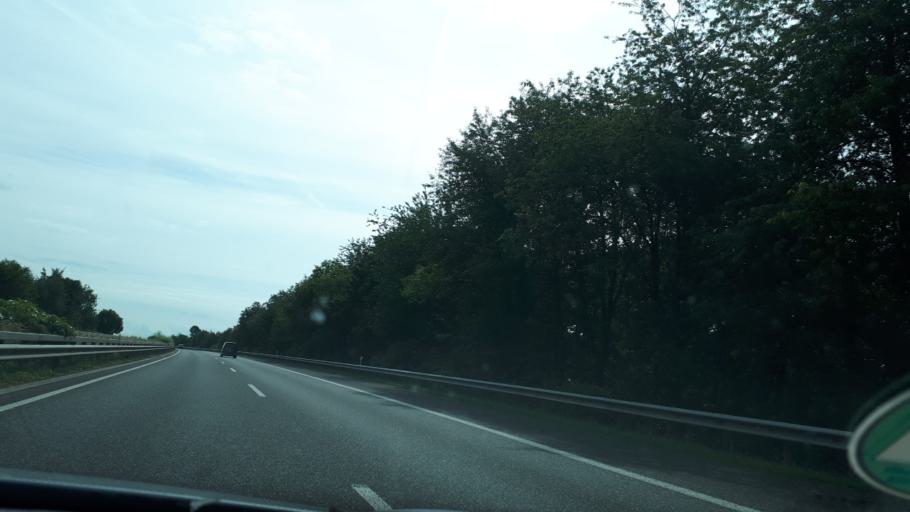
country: DE
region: Rheinland-Pfalz
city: Eulgem
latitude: 50.2259
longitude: 7.1650
